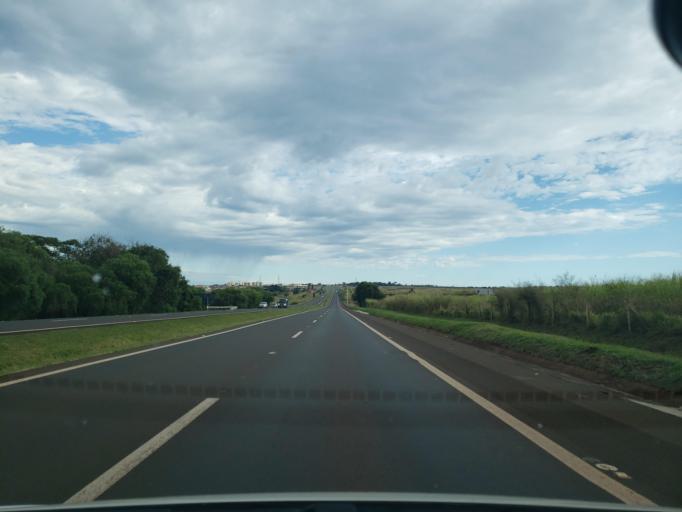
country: BR
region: Sao Paulo
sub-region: Jau
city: Jau
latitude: -22.2627
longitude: -48.5302
